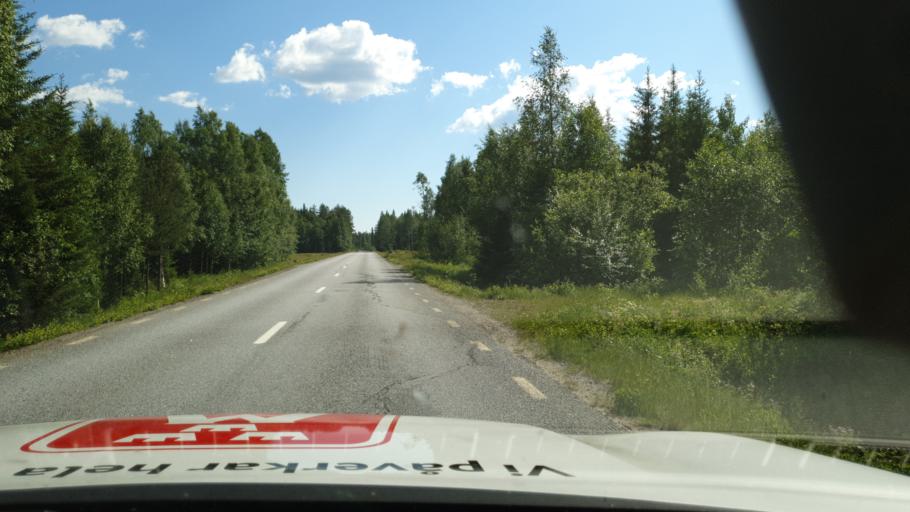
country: SE
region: Vaesterbotten
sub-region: Skelleftea Kommun
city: Burtraesk
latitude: 64.4454
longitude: 20.3958
